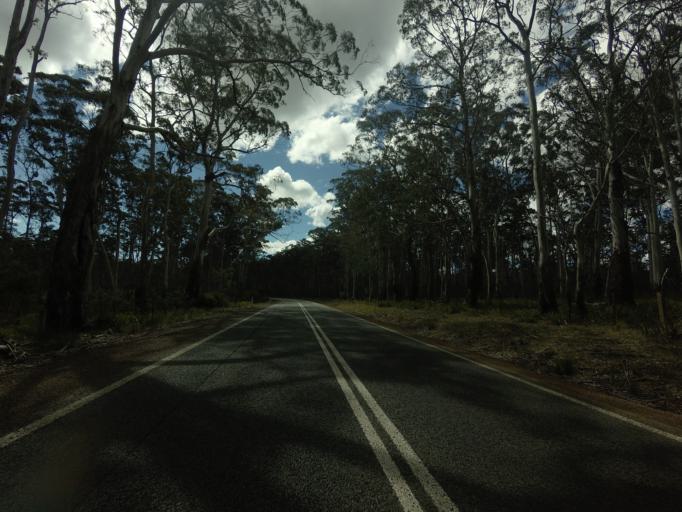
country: AU
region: Tasmania
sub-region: Northern Midlands
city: Evandale
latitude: -41.9704
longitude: 147.6472
